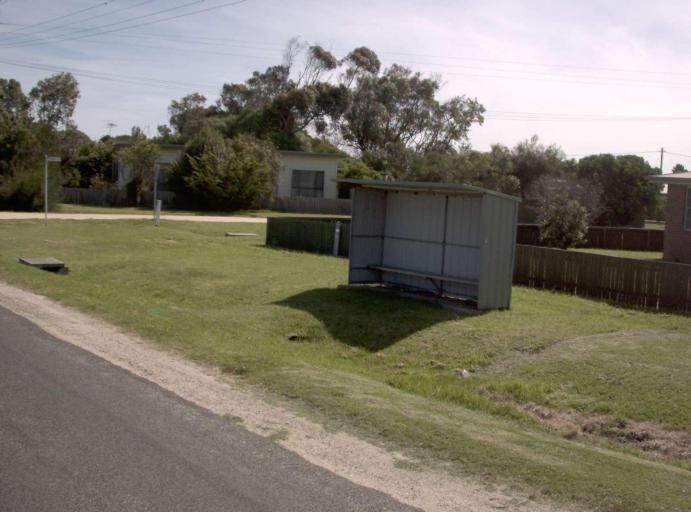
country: AU
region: Victoria
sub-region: Wellington
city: Sale
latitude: -38.3707
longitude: 147.1891
